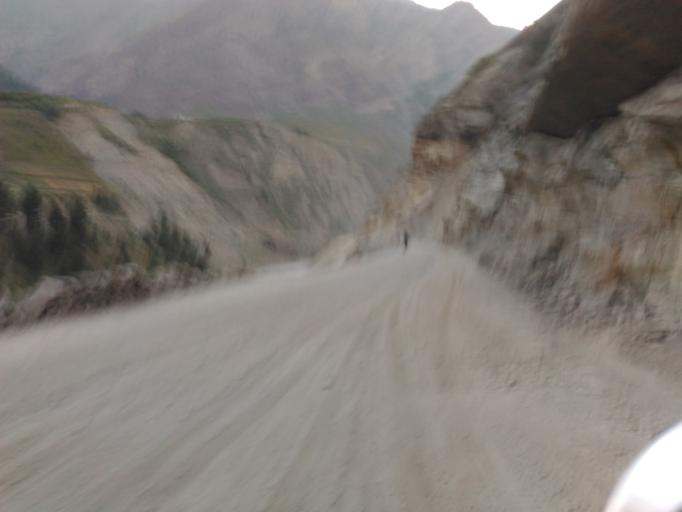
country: IN
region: Himachal Pradesh
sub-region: Lahul and Spiti
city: Kyelang
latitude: 32.5190
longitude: 76.9781
